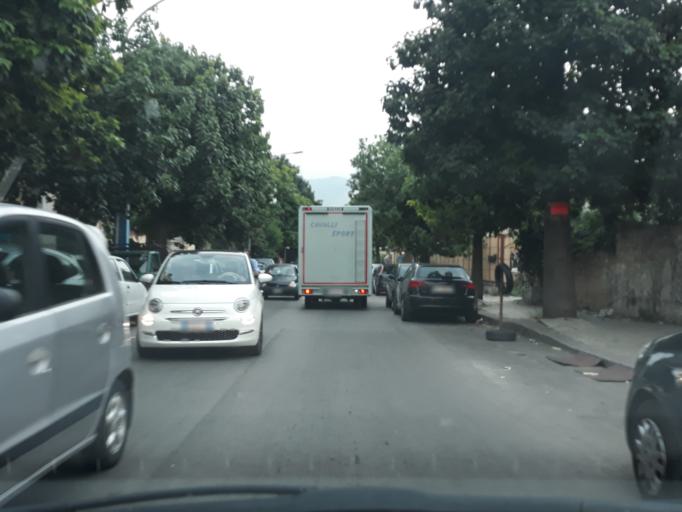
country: IT
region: Sicily
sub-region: Palermo
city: Monreale
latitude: 38.0960
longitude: 13.3188
